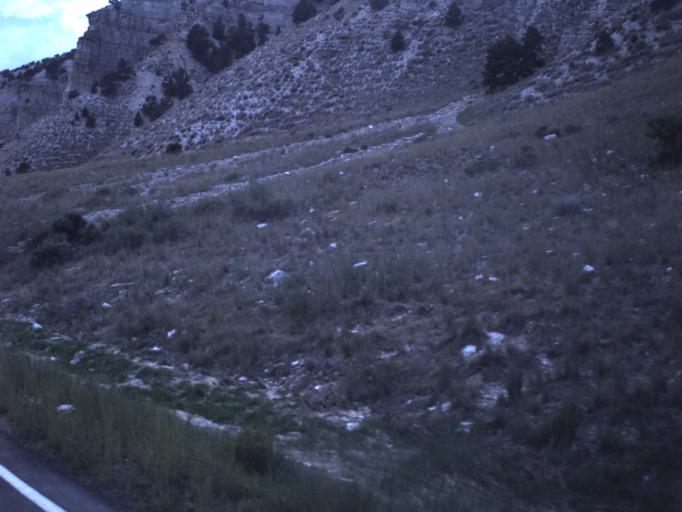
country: US
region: Utah
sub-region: Duchesne County
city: Duchesne
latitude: 40.0322
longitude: -110.5441
